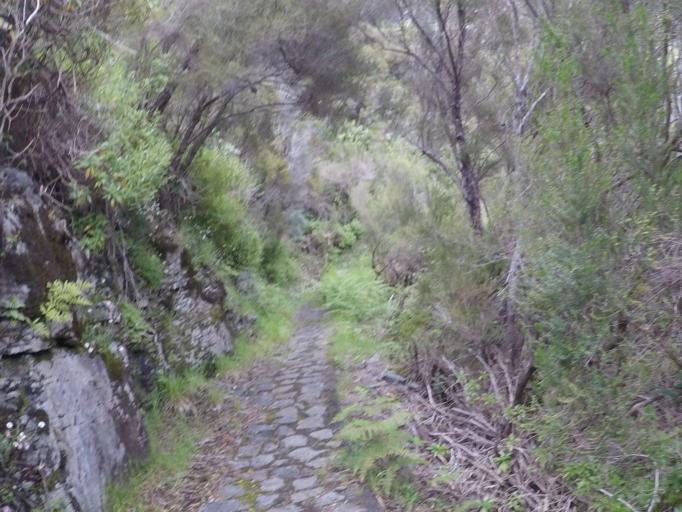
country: PT
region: Madeira
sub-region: Camara de Lobos
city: Curral das Freiras
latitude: 32.7347
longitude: -16.9979
